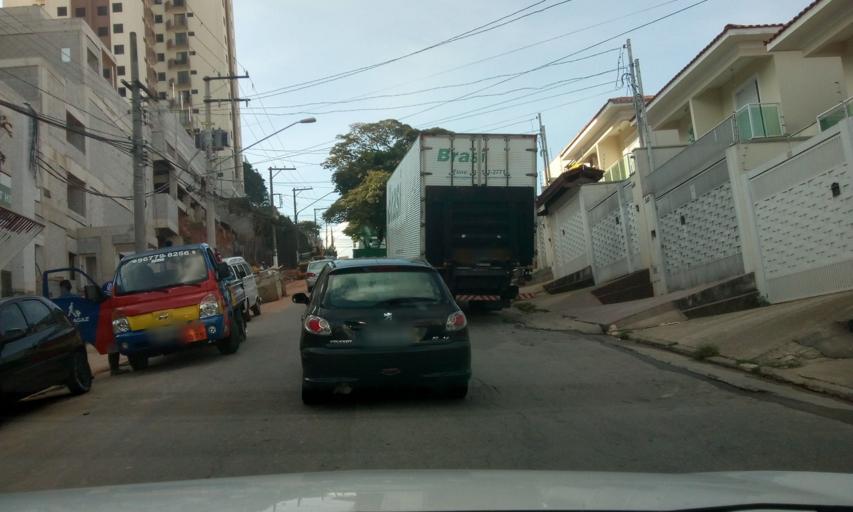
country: BR
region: Sao Paulo
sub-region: Sao Paulo
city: Sao Paulo
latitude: -23.4996
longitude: -46.6798
